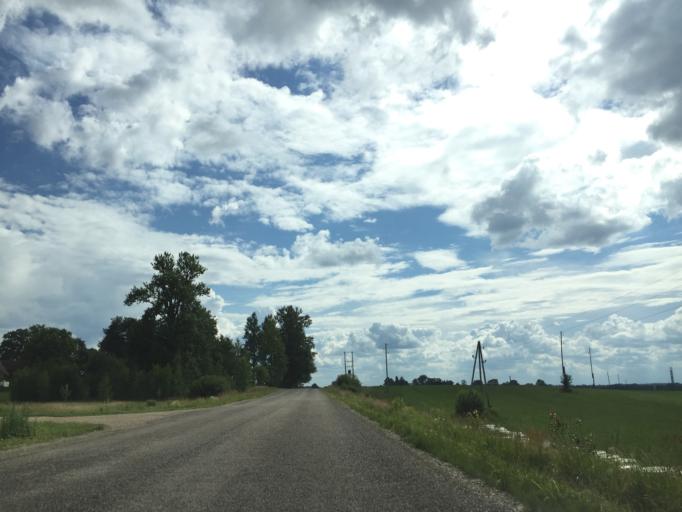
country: LV
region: Sigulda
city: Sigulda
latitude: 57.1798
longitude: 24.9268
